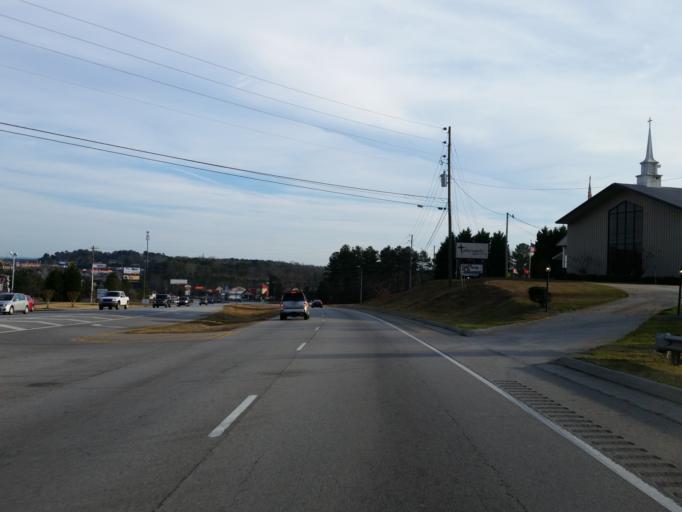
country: US
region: Georgia
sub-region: Paulding County
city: Hiram
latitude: 33.8988
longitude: -84.7688
